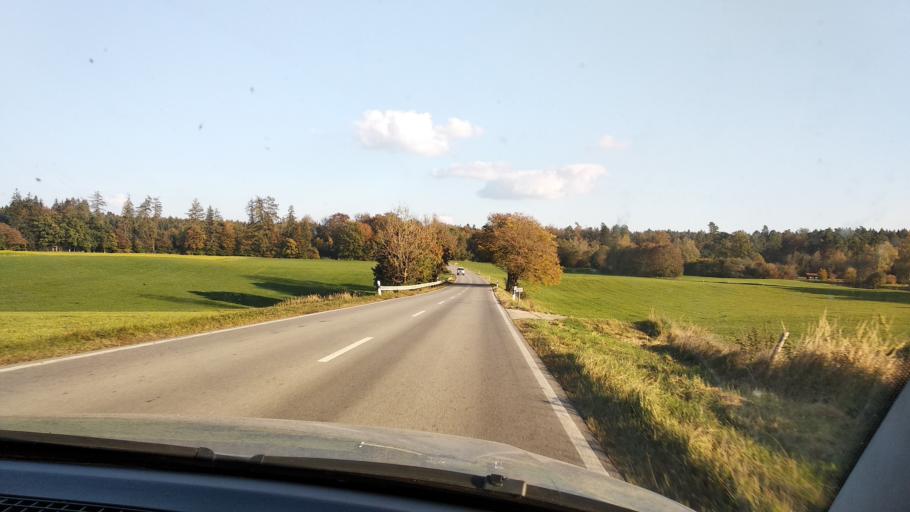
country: DE
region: Bavaria
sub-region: Upper Bavaria
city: Egmating
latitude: 48.0041
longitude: 11.8062
